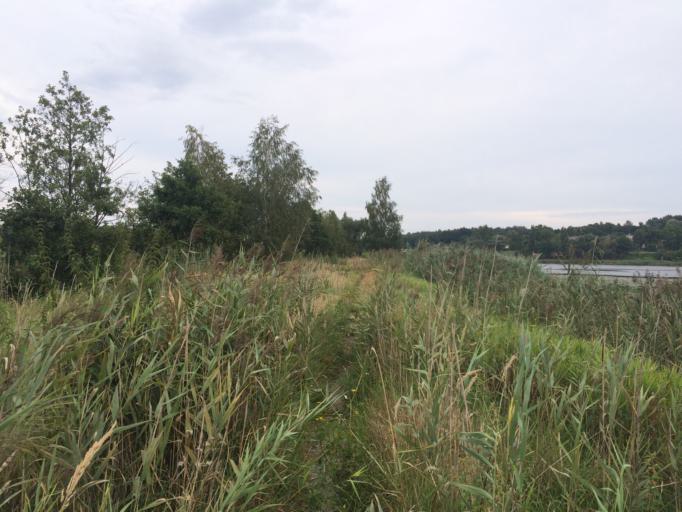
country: PL
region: Swietokrzyskie
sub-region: Powiat starachowicki
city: Starachowice
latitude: 51.0515
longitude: 21.0546
